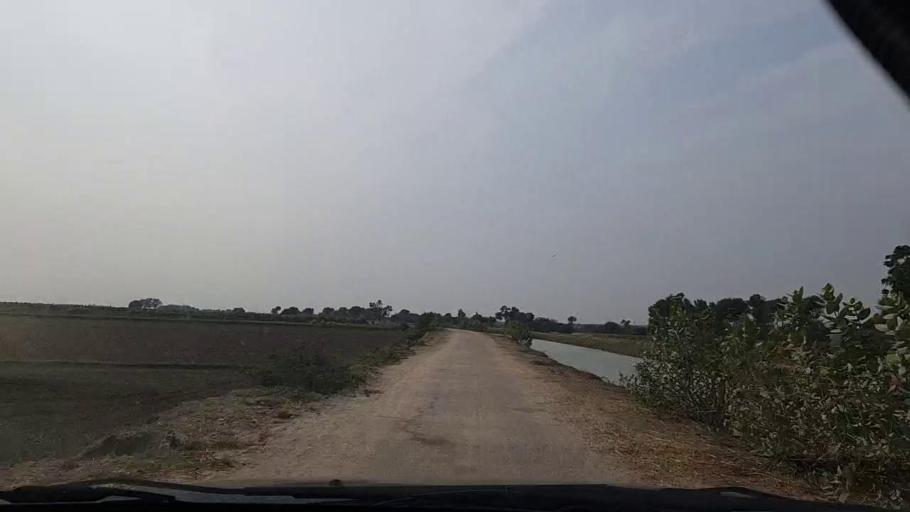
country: PK
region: Sindh
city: Thatta
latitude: 24.5774
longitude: 67.8846
